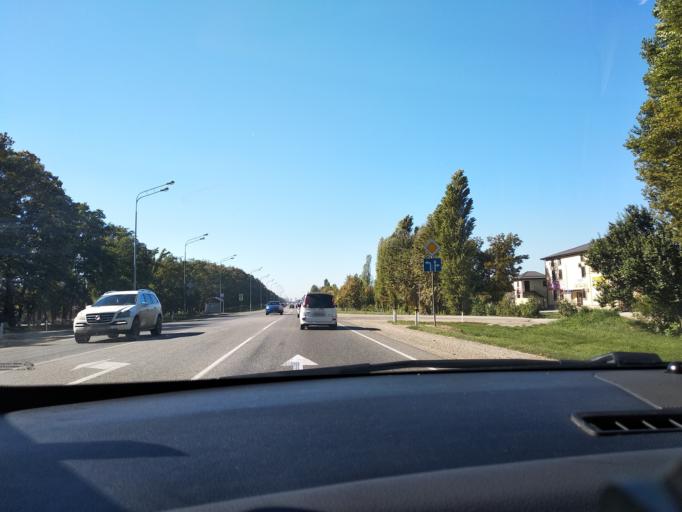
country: RU
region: Krasnodarskiy
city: Novotitarovskaya
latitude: 45.1465
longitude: 39.0508
